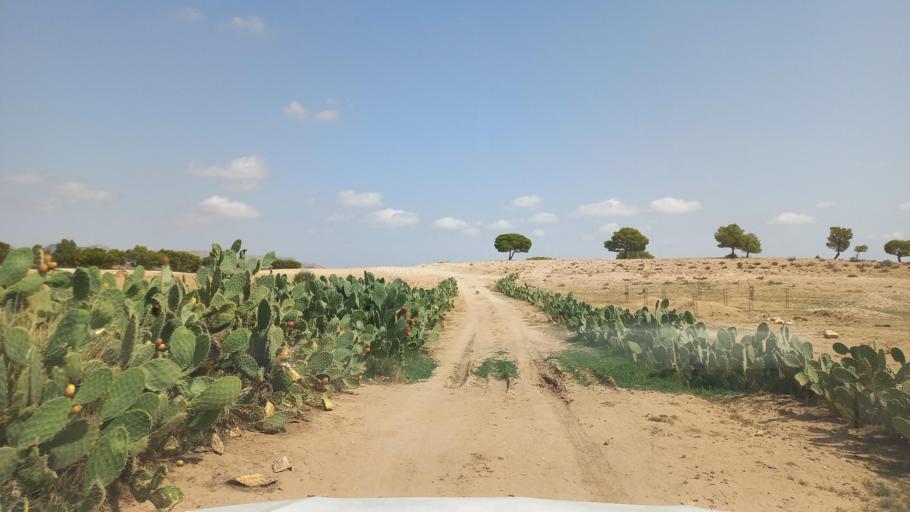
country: TN
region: Al Qasrayn
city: Sbiba
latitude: 35.3951
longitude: 8.9854
